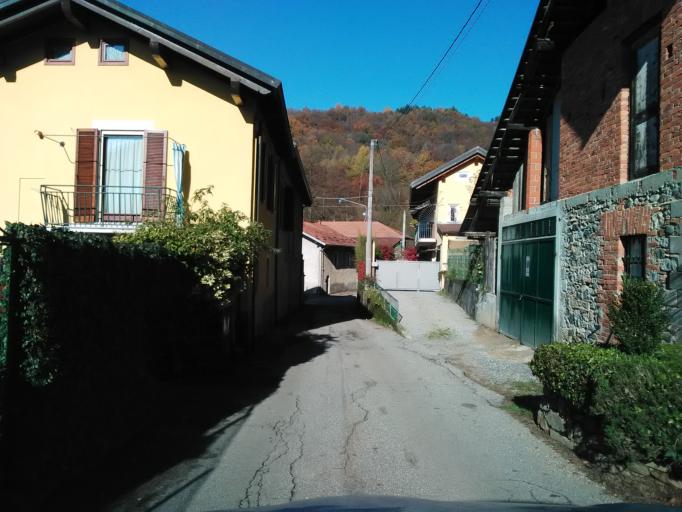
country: IT
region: Piedmont
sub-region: Provincia di Vercelli
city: Borgosesia
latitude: 45.7336
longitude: 8.2847
